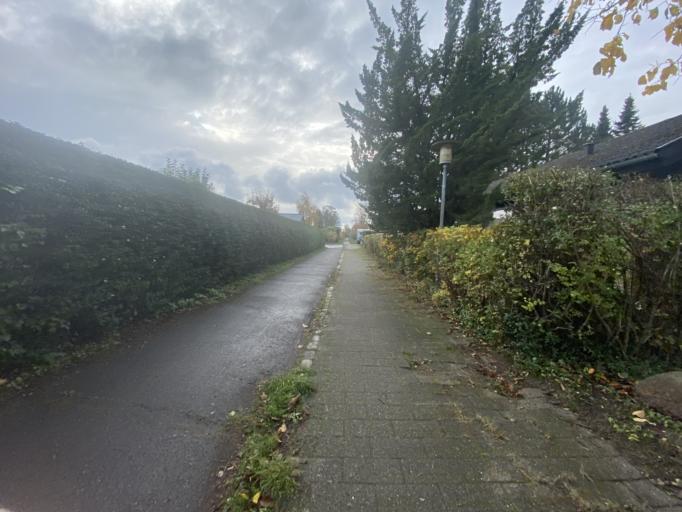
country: DK
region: Capital Region
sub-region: Dragor Kommune
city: Dragor
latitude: 55.5922
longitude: 12.6498
